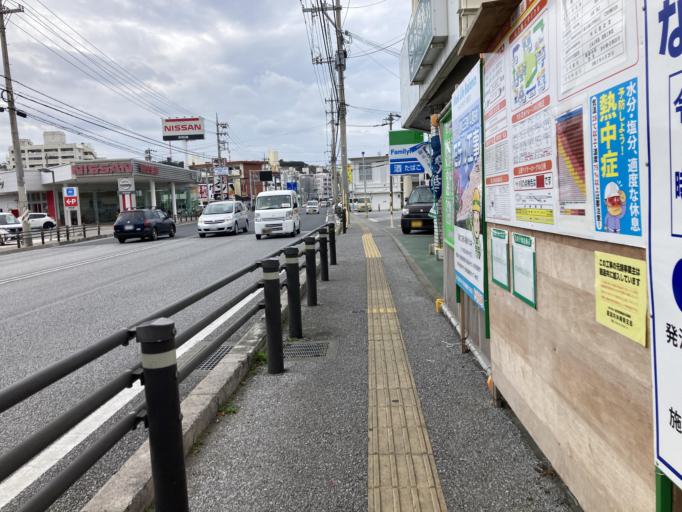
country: JP
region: Okinawa
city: Tomigusuku
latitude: 26.1973
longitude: 127.7069
